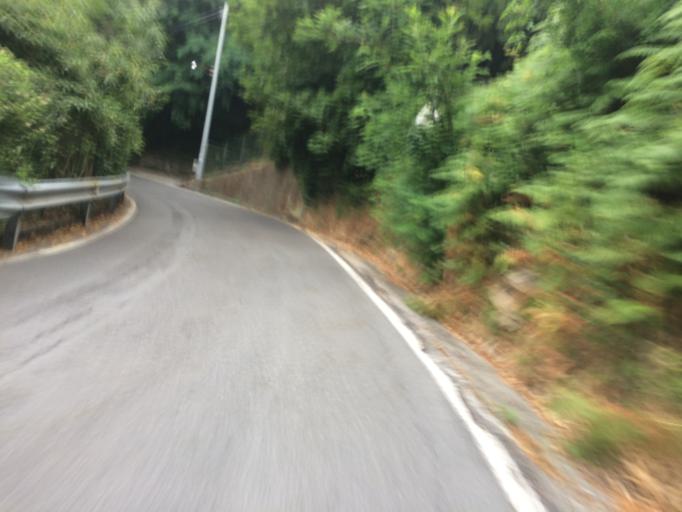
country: IT
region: Liguria
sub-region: Provincia di Imperia
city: Seborga
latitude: 43.8538
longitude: 7.7283
